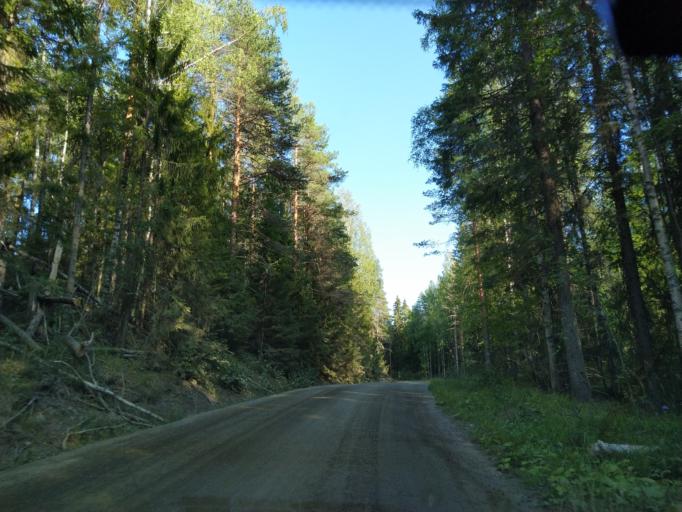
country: FI
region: Central Finland
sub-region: Jaemsae
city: Kuhmoinen
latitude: 61.6815
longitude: 24.9783
